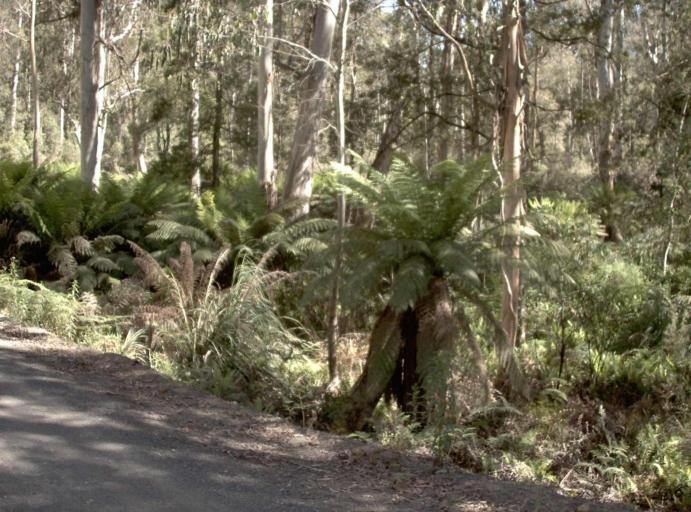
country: AU
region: New South Wales
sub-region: Bombala
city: Bombala
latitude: -37.2217
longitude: 148.7477
